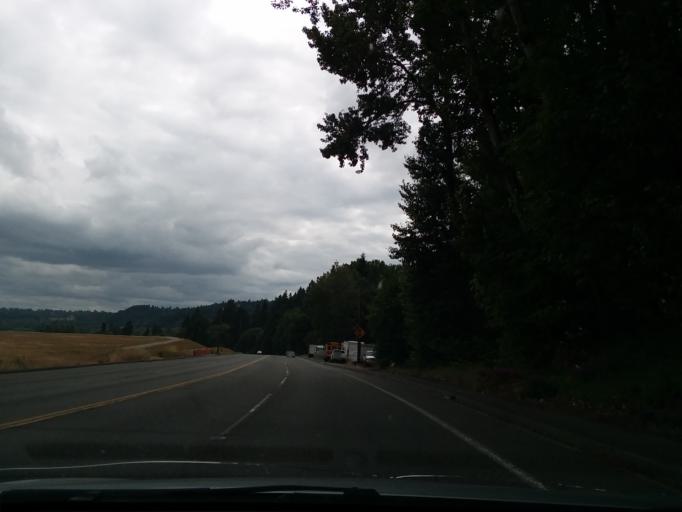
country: US
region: Washington
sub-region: King County
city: SeaTac
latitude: 47.4269
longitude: -122.2752
